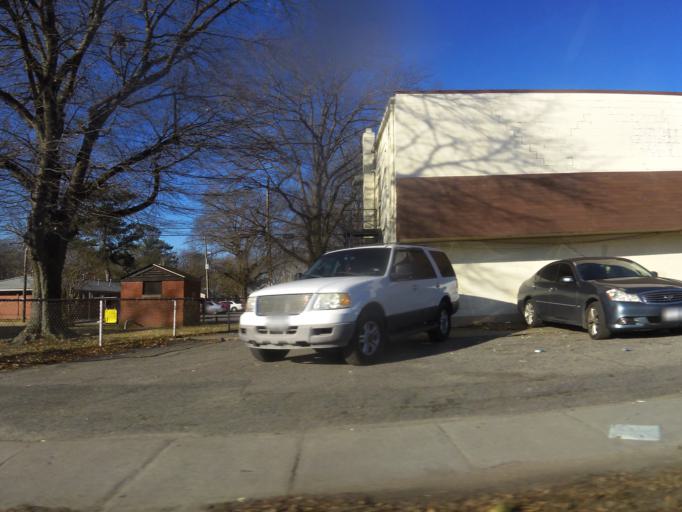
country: US
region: Virginia
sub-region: City of Hopewell
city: Hopewell
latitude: 37.3010
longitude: -77.2927
